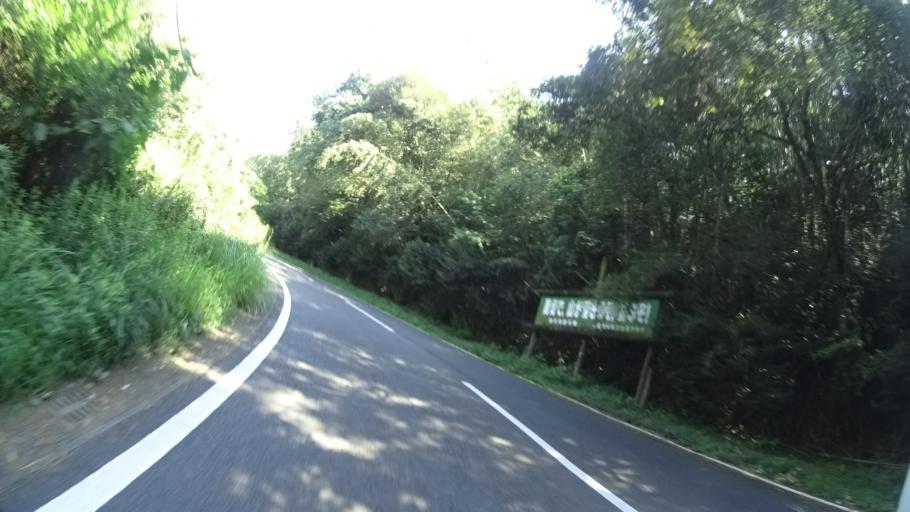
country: JP
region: Kagoshima
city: Kajiki
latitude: 31.7549
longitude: 130.6678
